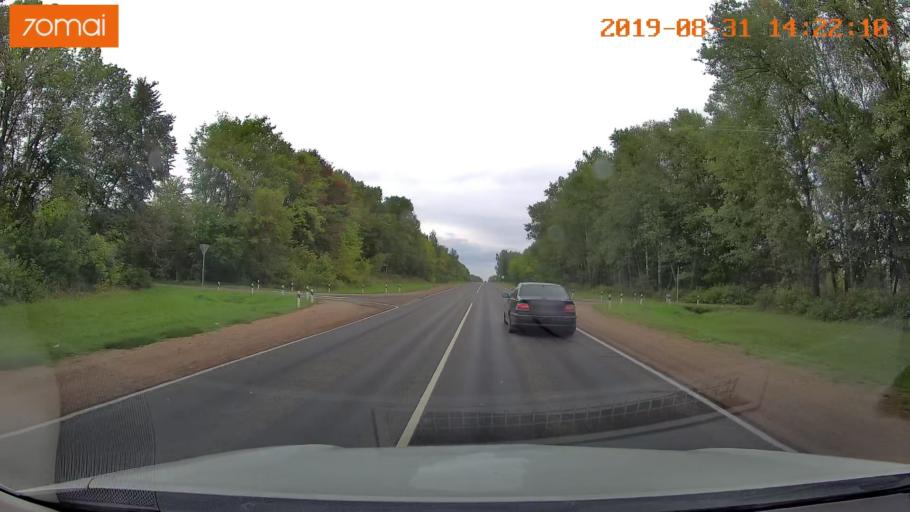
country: RU
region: Smolensk
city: Yekimovichi
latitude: 54.0900
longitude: 33.2122
